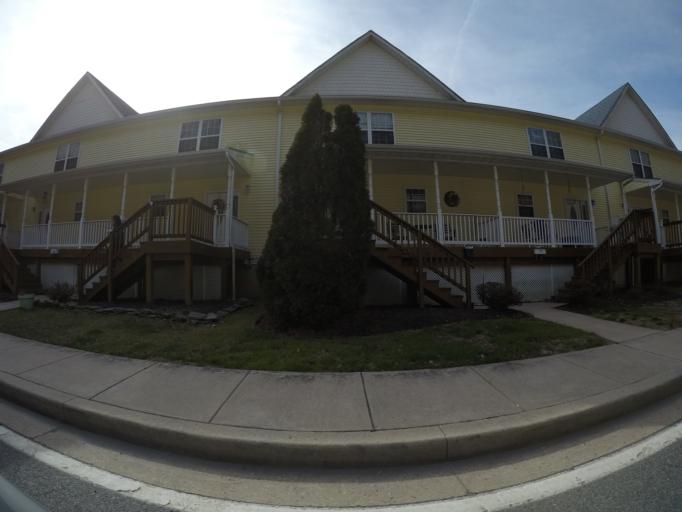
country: US
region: Maryland
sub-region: Harford County
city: Havre de Grace
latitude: 39.6090
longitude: -76.1198
